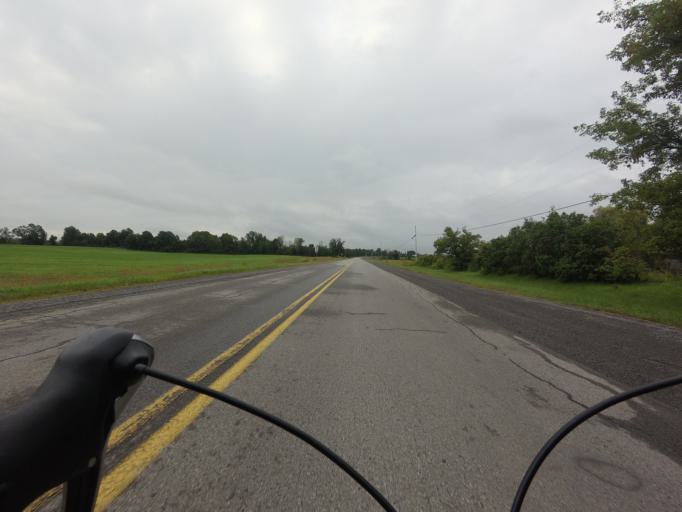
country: CA
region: Ontario
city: Bells Corners
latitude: 45.1719
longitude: -75.8107
